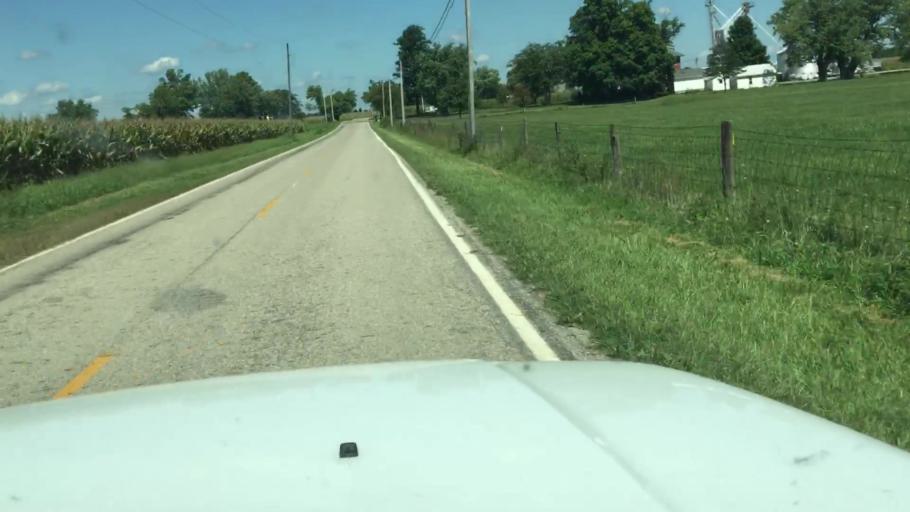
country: US
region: Ohio
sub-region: Madison County
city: Mount Sterling
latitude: 39.6586
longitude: -83.2373
